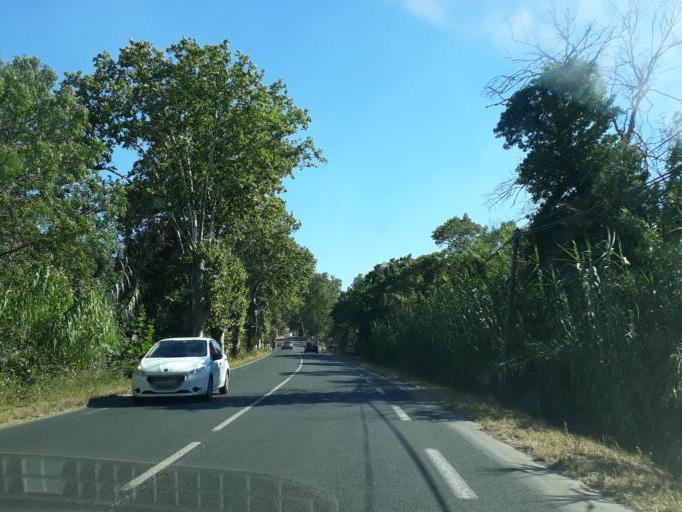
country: FR
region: Languedoc-Roussillon
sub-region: Departement de l'Herault
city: Agde
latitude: 43.3210
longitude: 3.4763
